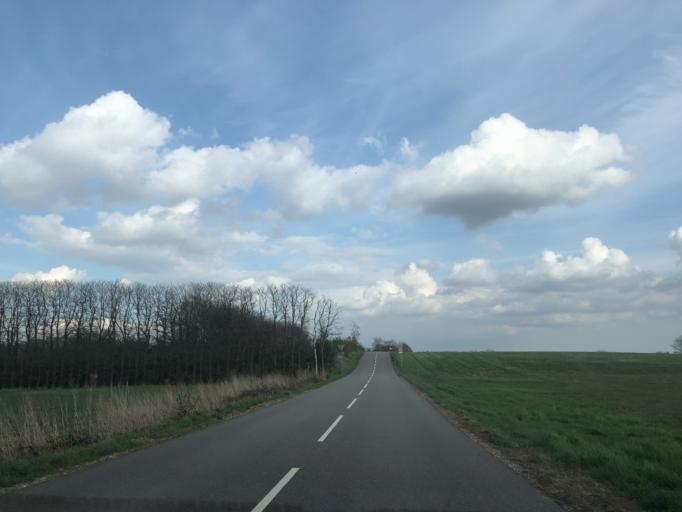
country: DK
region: Zealand
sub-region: Roskilde Kommune
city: Gundsomagle
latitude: 55.7158
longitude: 12.1147
